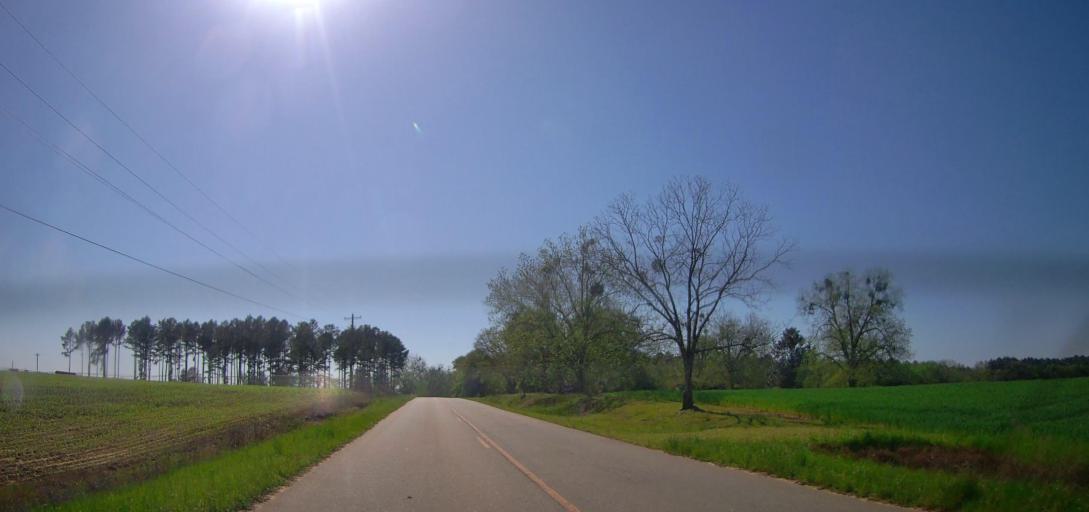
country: US
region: Georgia
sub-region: Pulaski County
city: Hawkinsville
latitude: 32.2407
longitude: -83.5563
